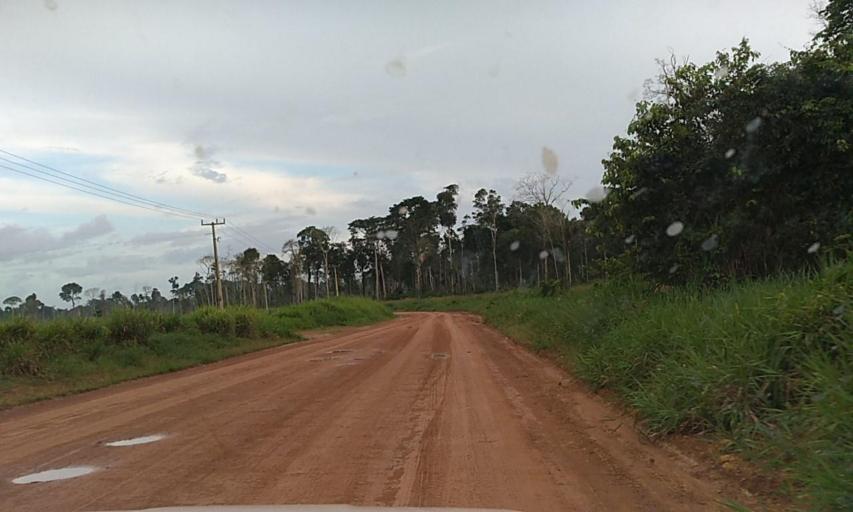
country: BR
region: Para
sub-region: Senador Jose Porfirio
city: Senador Jose Porfirio
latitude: -2.7052
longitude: -51.8125
